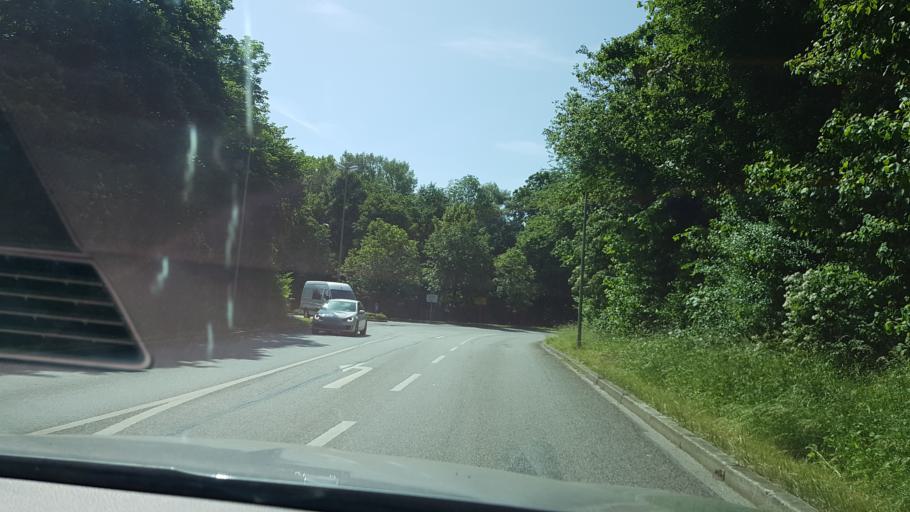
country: DE
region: Bavaria
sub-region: Upper Bavaria
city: Fuerstenfeldbruck
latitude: 48.1833
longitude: 11.2681
